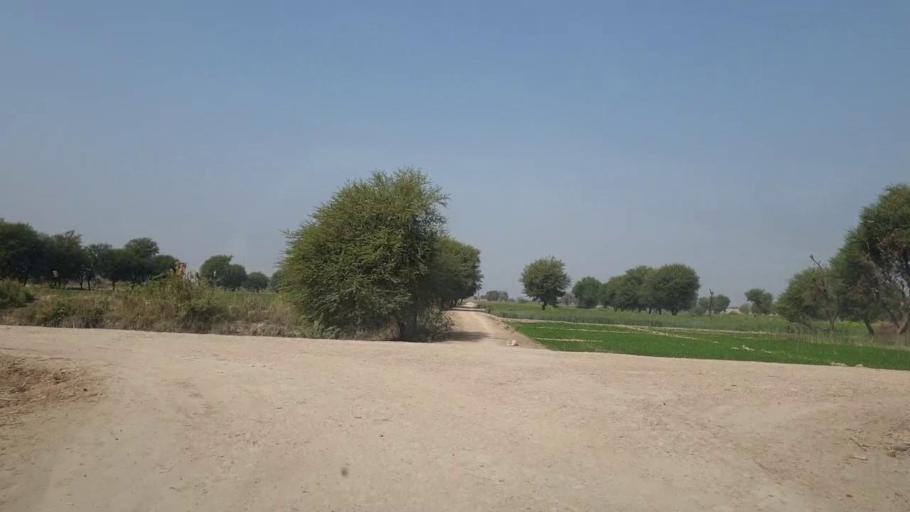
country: PK
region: Sindh
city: Mirpur Khas
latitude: 25.6581
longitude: 69.1333
